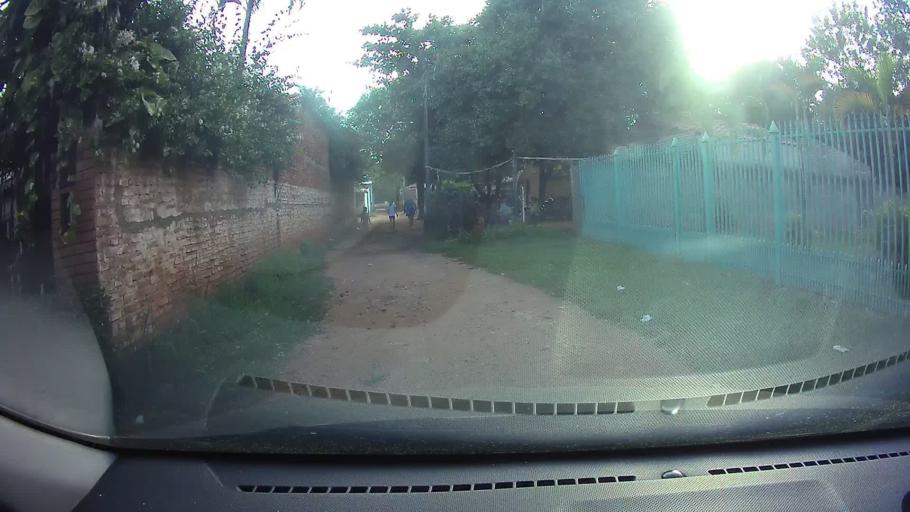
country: PY
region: Central
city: San Lorenzo
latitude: -25.2770
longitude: -57.4877
